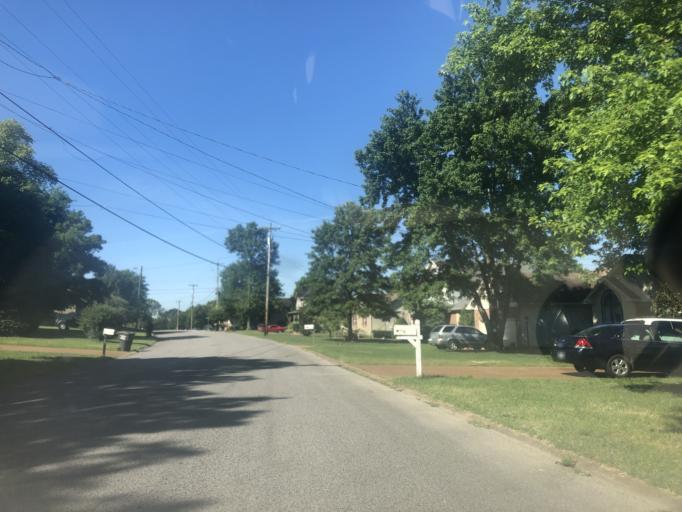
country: US
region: Tennessee
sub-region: Davidson County
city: Lakewood
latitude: 36.2411
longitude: -86.6684
